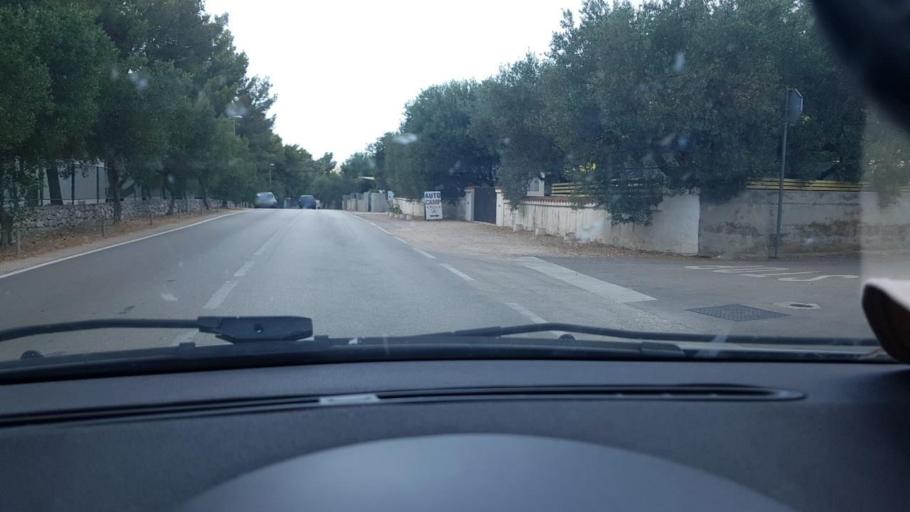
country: HR
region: Sibensko-Kniniska
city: Vodice
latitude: 43.7536
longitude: 15.7901
